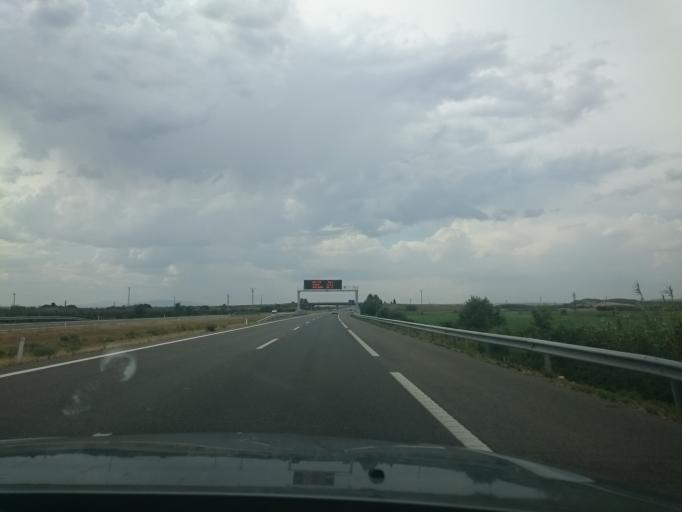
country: ES
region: Navarre
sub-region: Provincia de Navarra
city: Murchante
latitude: 42.0219
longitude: -1.6205
